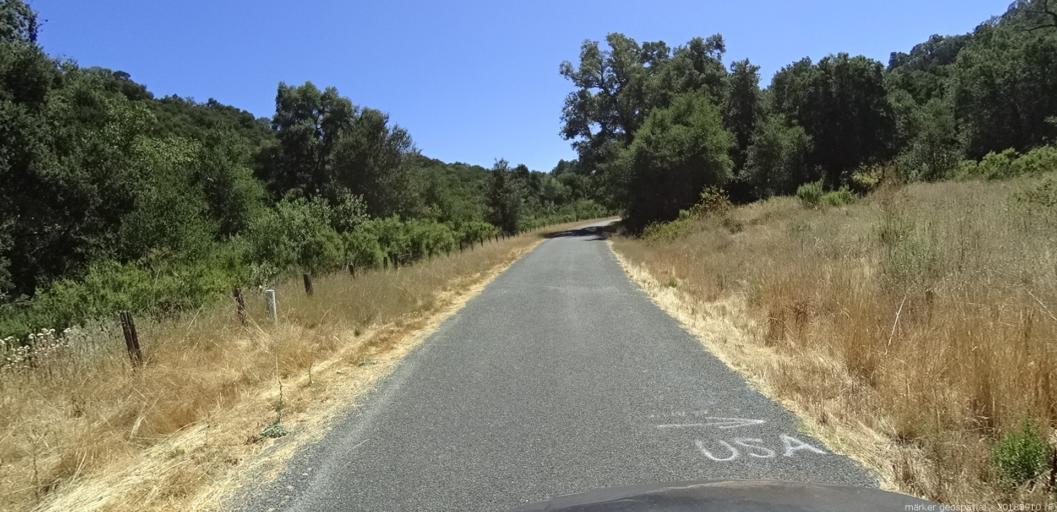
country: US
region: California
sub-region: Monterey County
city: Carmel Valley Village
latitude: 36.4365
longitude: -121.7934
